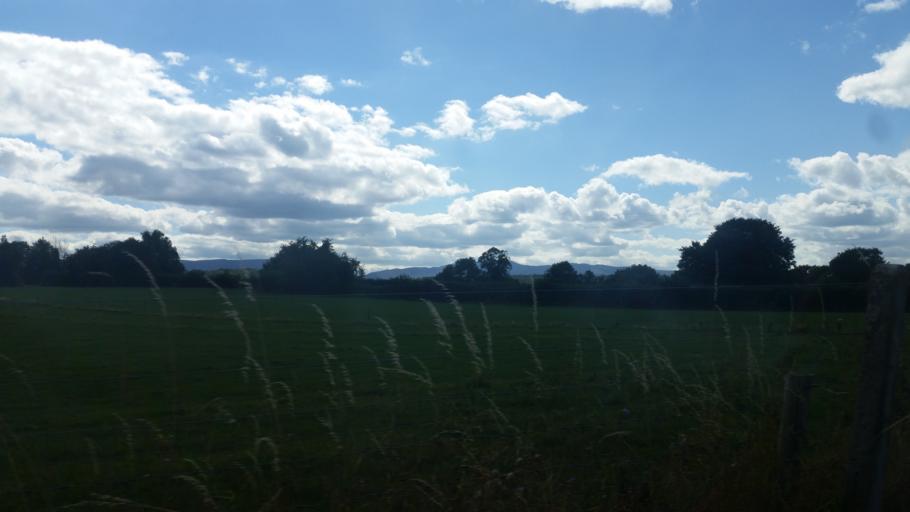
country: IE
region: Munster
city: Carrick-on-Suir
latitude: 52.3596
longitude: -7.4288
